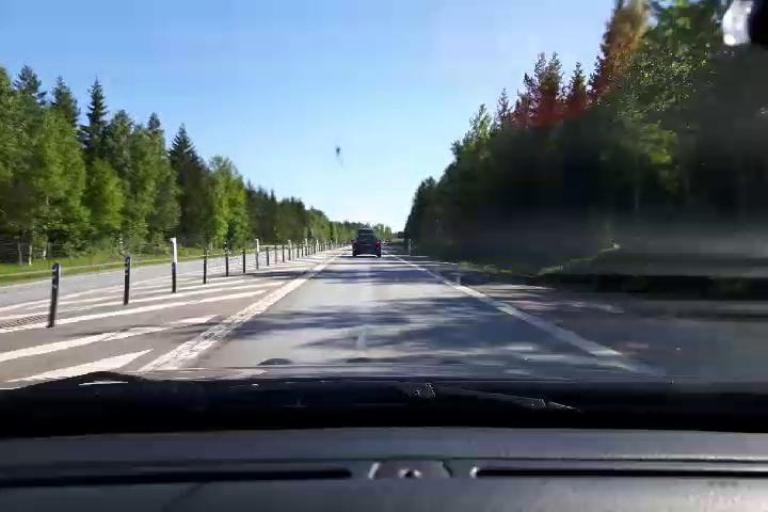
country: SE
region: Gaevleborg
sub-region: Gavle Kommun
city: Norrsundet
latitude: 60.8265
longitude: 17.0838
